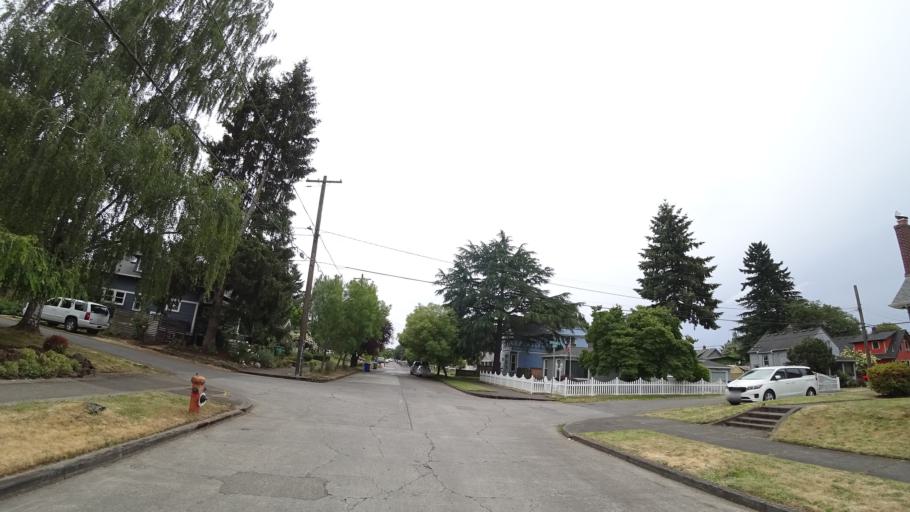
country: US
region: Oregon
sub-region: Multnomah County
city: Portland
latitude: 45.5760
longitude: -122.6993
